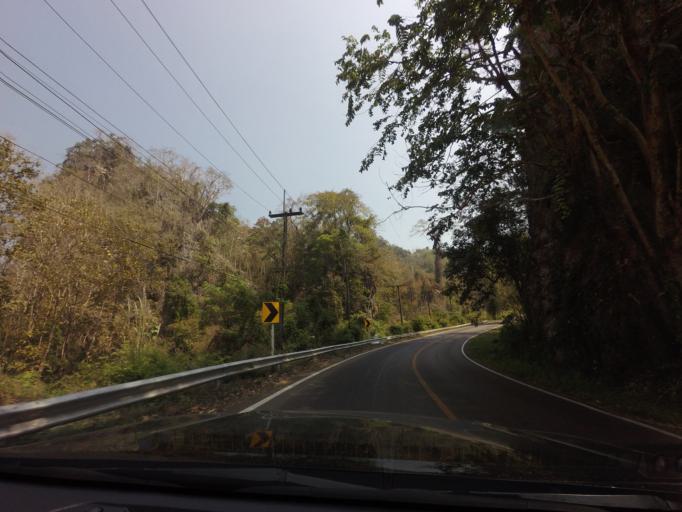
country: TH
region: Kanchanaburi
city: Thong Pha Phum
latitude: 14.7768
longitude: 98.5765
